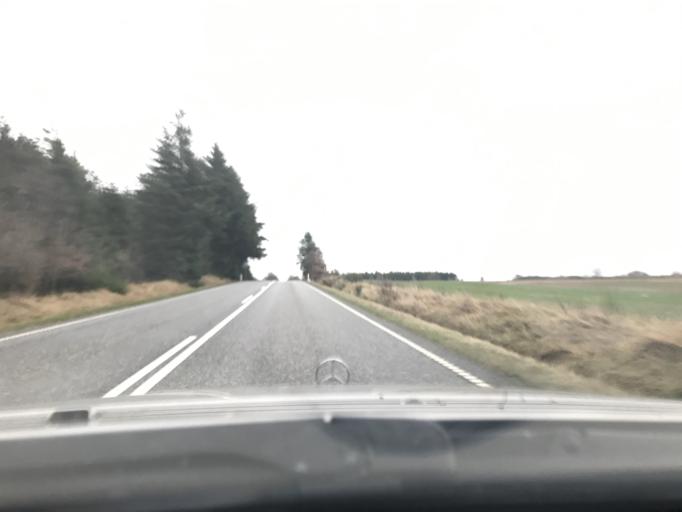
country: DK
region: South Denmark
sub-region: Tonder Kommune
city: Logumkloster
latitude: 55.1727
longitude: 8.9495
